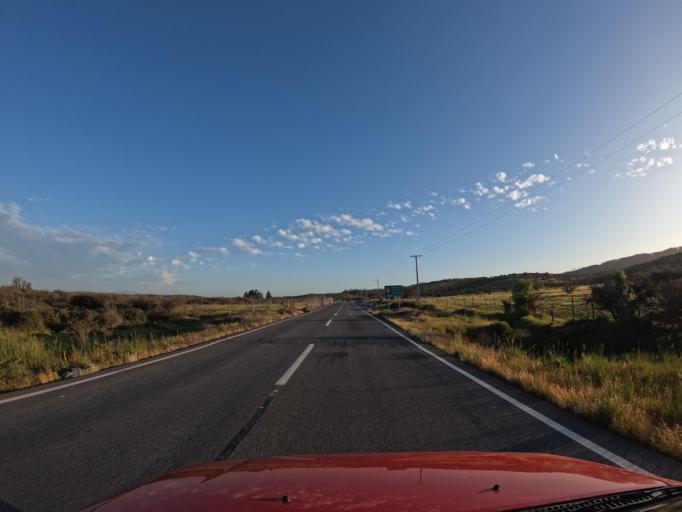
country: CL
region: O'Higgins
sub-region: Provincia de Colchagua
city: Santa Cruz
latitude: -34.3236
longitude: -71.7438
